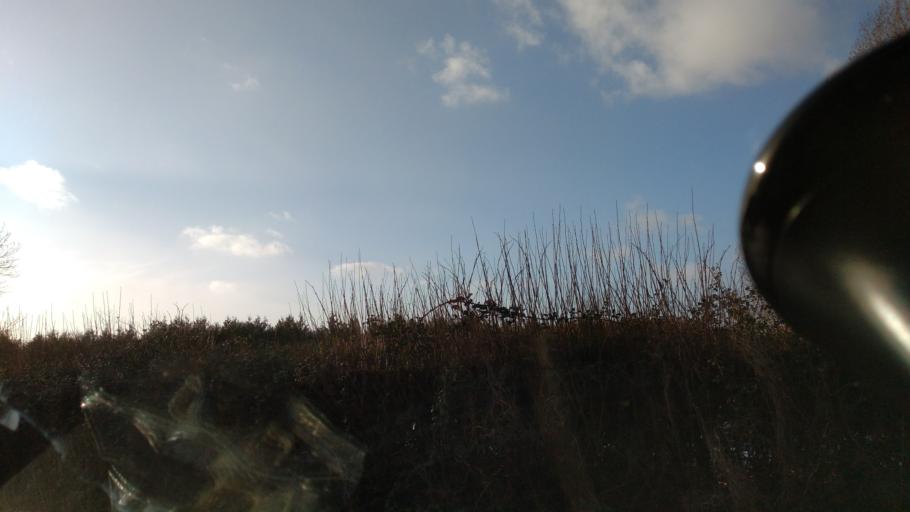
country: GB
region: England
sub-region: Somerset
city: Evercreech
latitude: 51.1382
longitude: -2.5500
